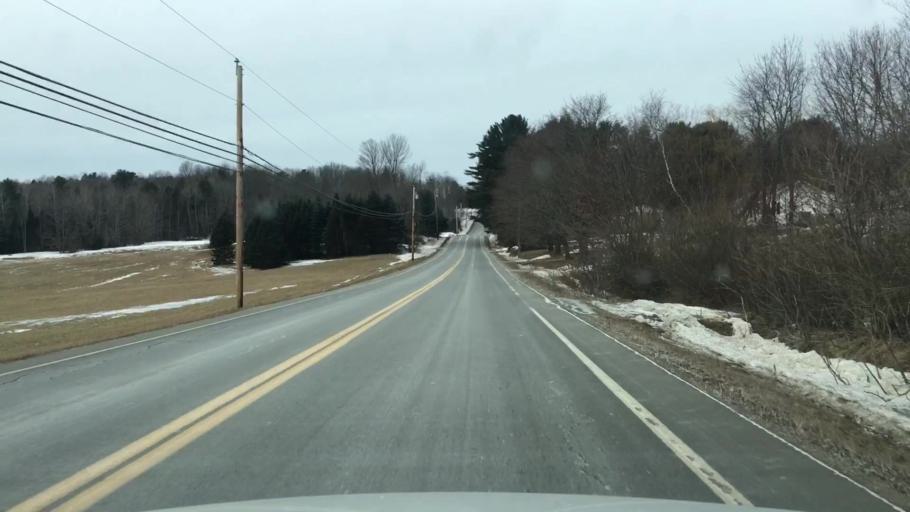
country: US
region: Maine
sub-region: Lincoln County
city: Whitefield
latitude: 44.2263
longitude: -69.6085
